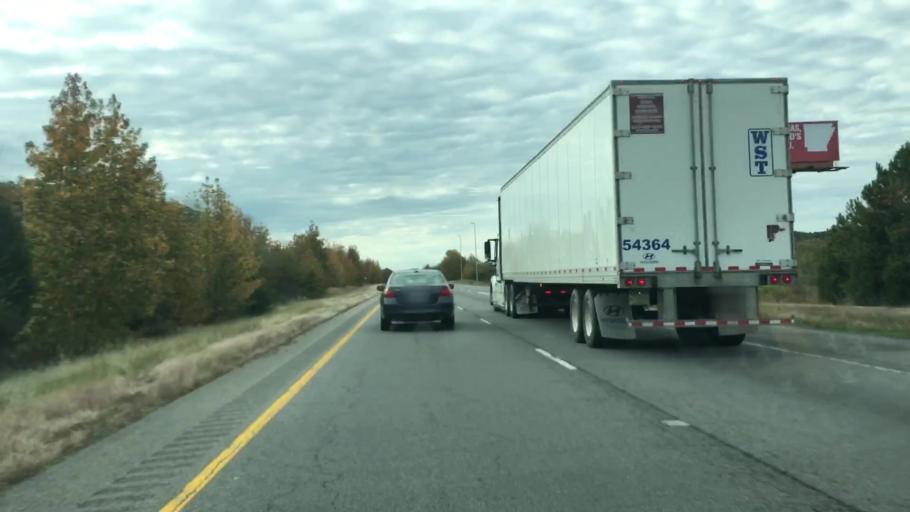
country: US
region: Arkansas
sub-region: Faulkner County
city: Conway
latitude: 35.1195
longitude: -92.4645
